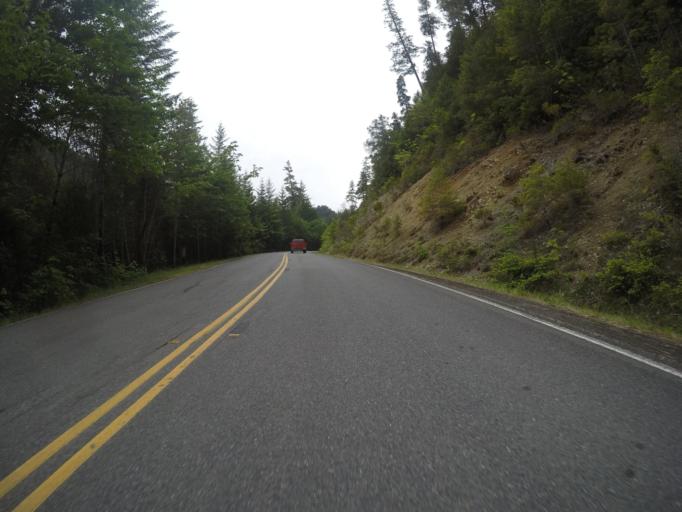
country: US
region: California
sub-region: Del Norte County
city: Bertsch-Oceanview
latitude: 41.7214
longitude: -123.9499
